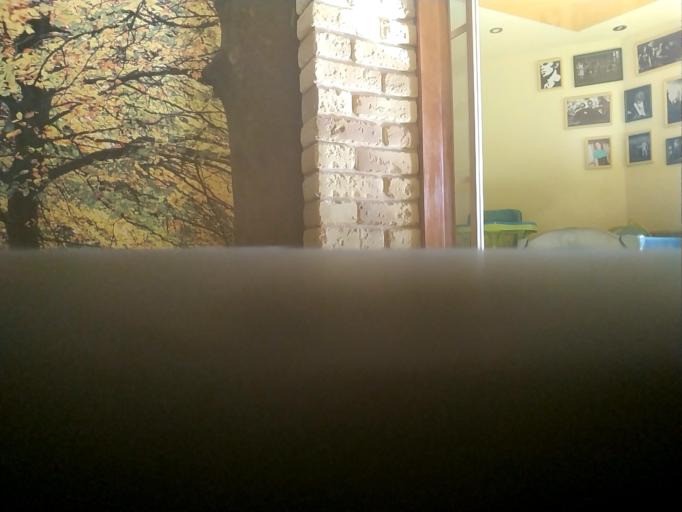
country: RU
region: Smolensk
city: Temkino
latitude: 54.9846
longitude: 34.9436
